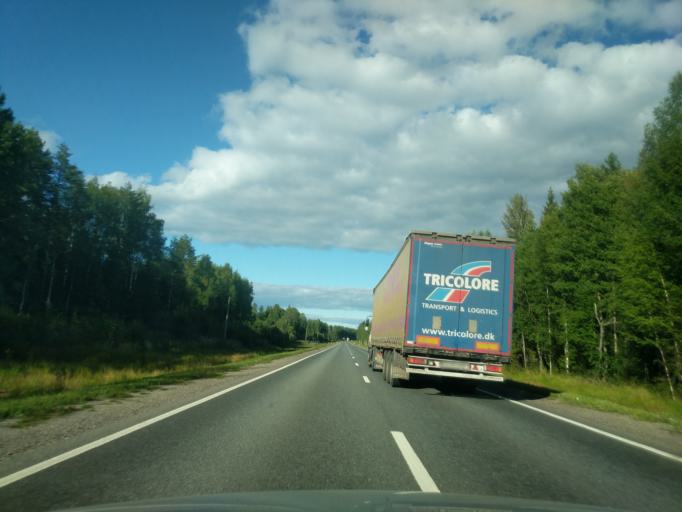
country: RU
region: Kostroma
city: Manturovo
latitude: 58.1487
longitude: 44.3702
